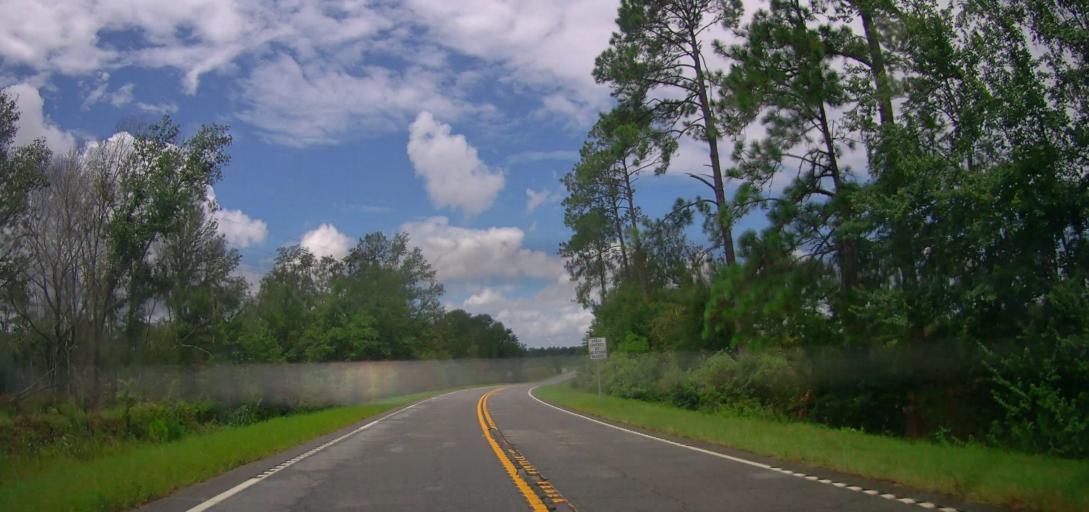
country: US
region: Georgia
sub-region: Wilcox County
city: Rochelle
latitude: 32.0364
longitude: -83.6098
